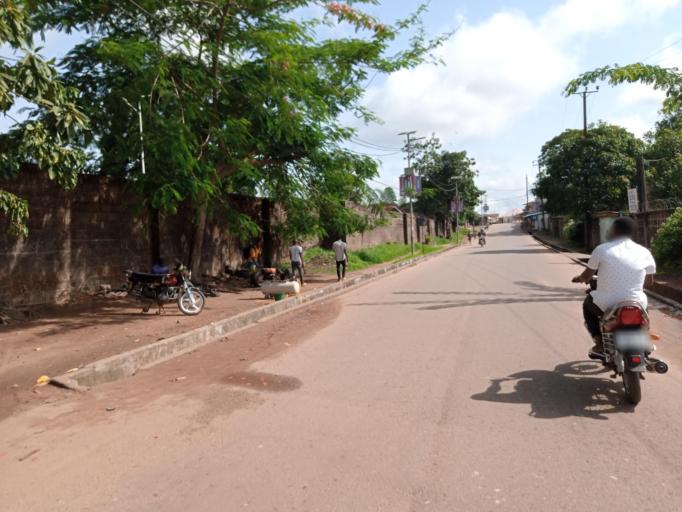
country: SL
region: Southern Province
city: Bo
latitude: 7.9623
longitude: -11.7415
